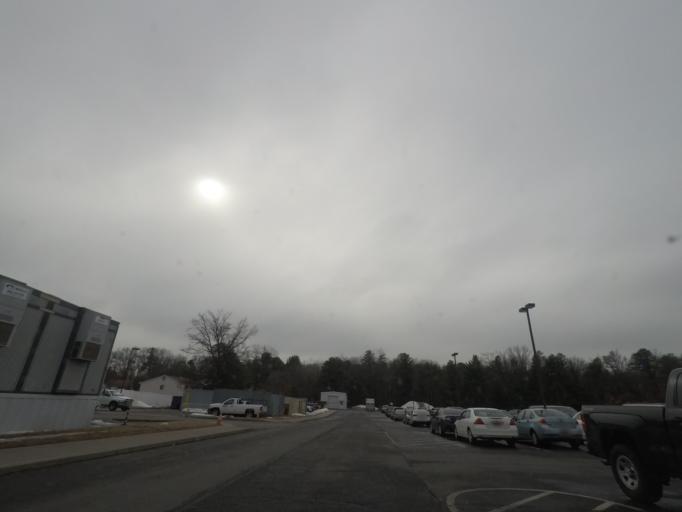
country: US
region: New York
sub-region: Albany County
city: McKownville
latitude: 42.6911
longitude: -73.8358
